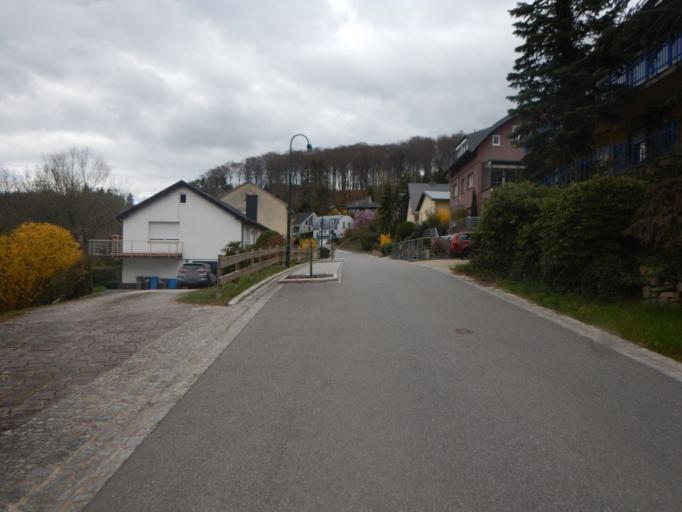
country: LU
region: Luxembourg
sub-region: Canton de Mersch
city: Lorentzweiler
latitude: 49.7049
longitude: 6.1435
